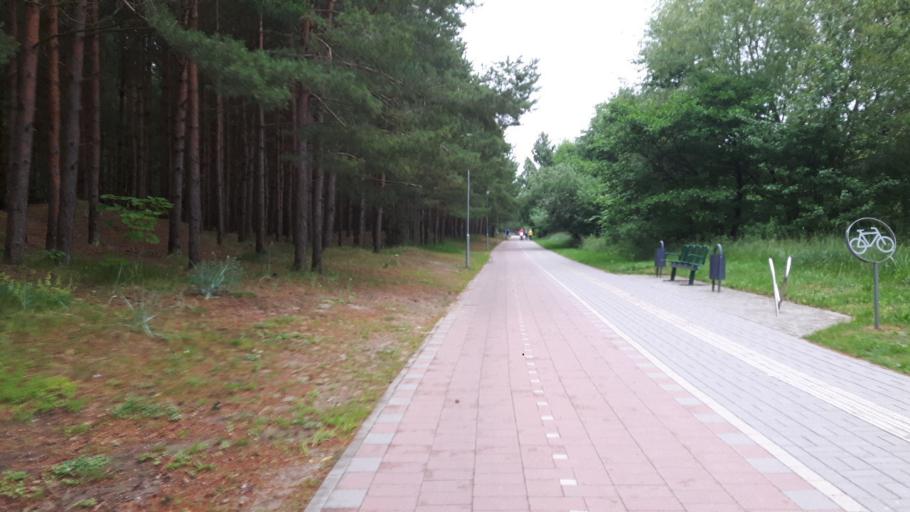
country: LV
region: Liepaja
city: Liepaja
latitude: 56.4913
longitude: 20.9981
